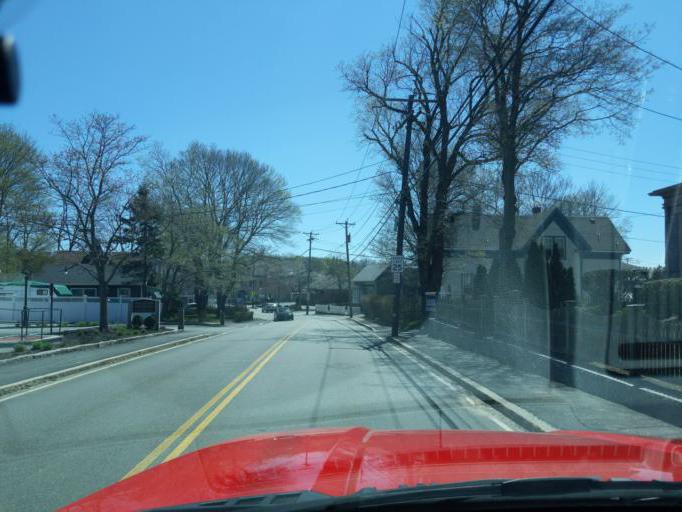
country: US
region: Massachusetts
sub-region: Essex County
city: Rockport
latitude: 42.6574
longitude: -70.6263
